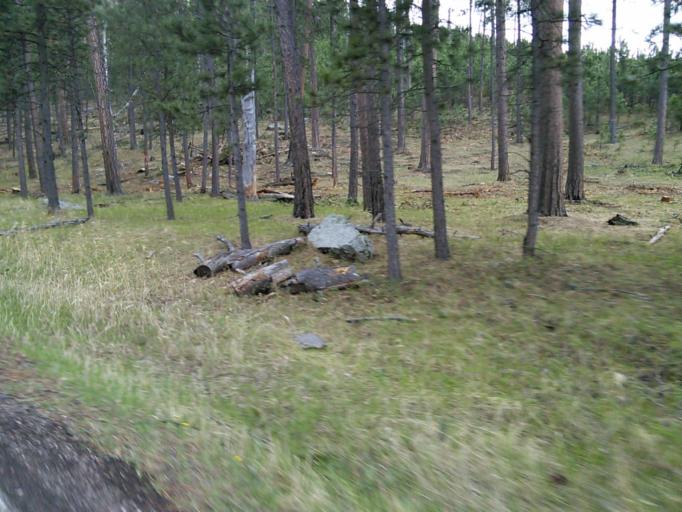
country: US
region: South Dakota
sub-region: Custer County
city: Custer
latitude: 43.7297
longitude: -103.4901
